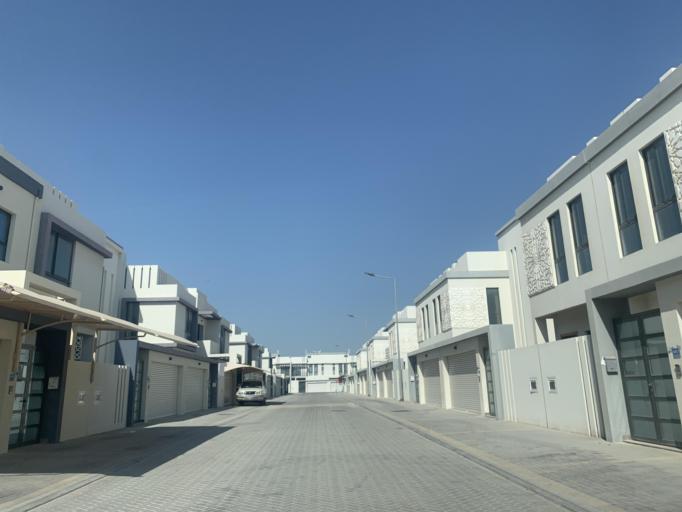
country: BH
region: Central Governorate
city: Madinat Hamad
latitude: 26.1301
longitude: 50.4839
